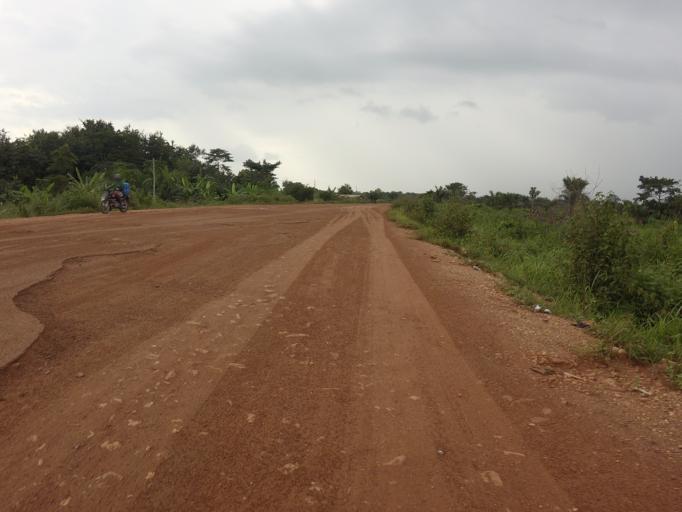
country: GH
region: Volta
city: Kpandu
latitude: 7.0071
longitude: 0.4302
